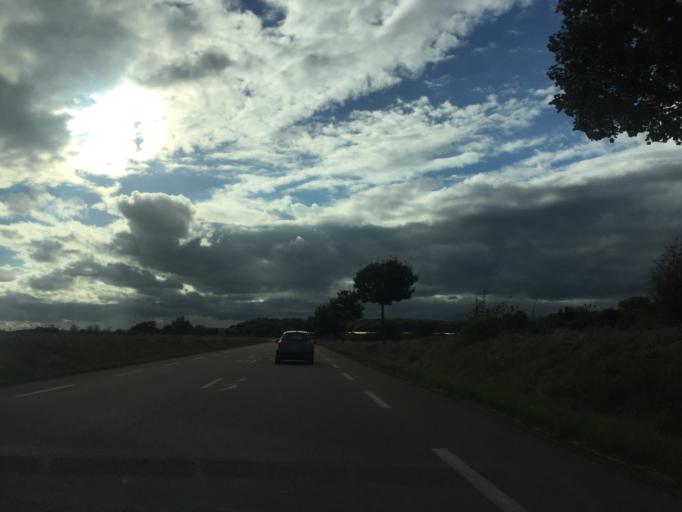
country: FR
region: Lorraine
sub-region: Departement des Vosges
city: Chatenois
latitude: 48.3041
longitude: 5.9209
